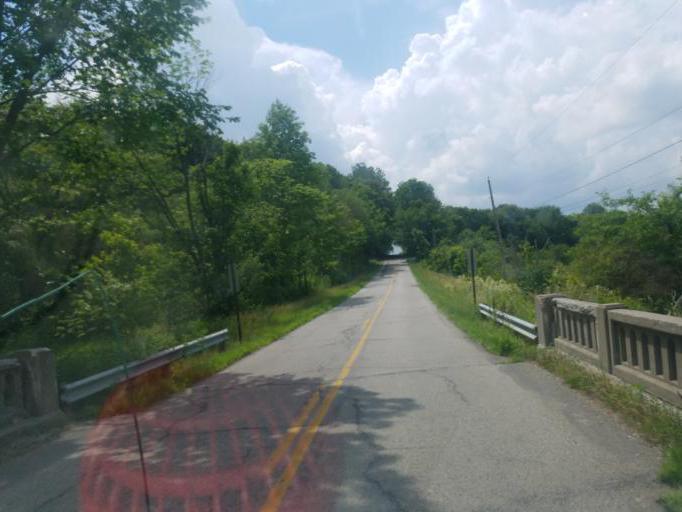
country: US
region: Ohio
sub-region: Mahoning County
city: Canfield
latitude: 40.9729
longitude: -80.8216
